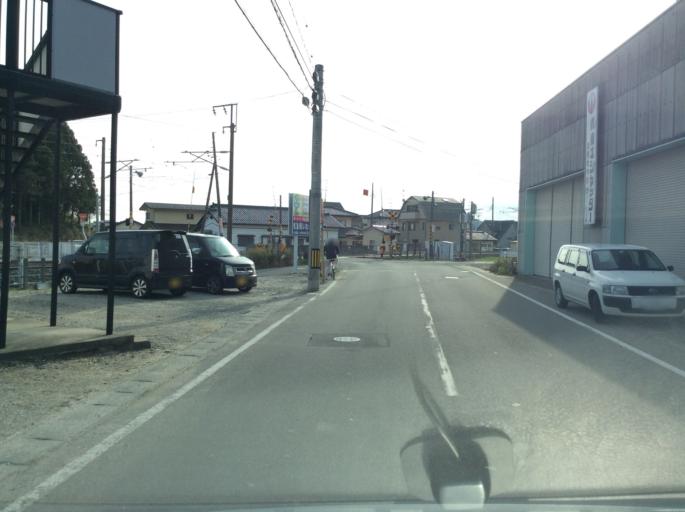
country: JP
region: Fukushima
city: Iwaki
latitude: 37.0710
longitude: 140.9426
